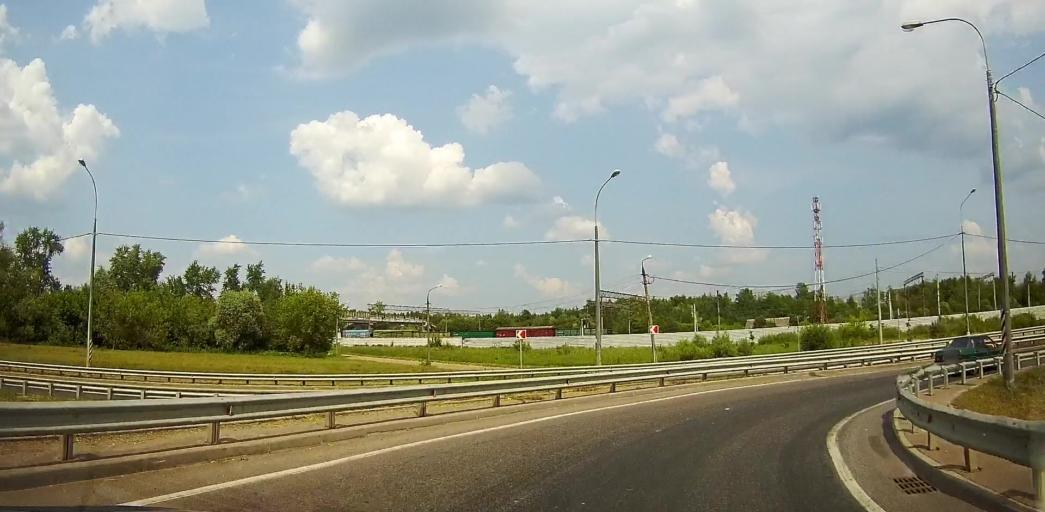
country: RU
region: Moskovskaya
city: Stupino
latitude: 54.9060
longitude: 38.0790
